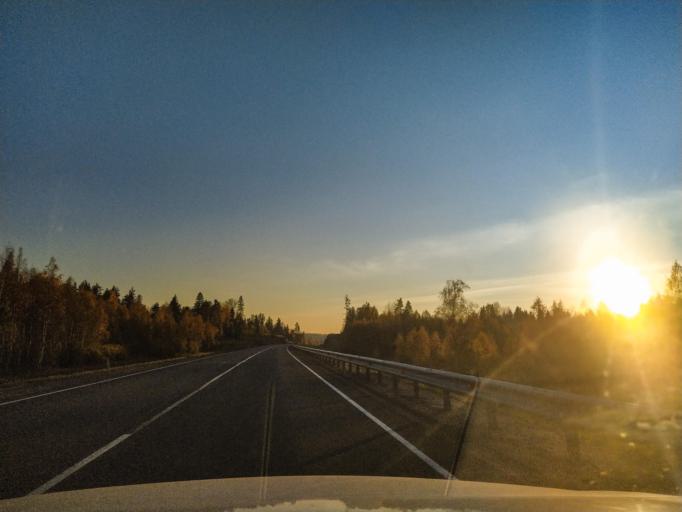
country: RU
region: Leningrad
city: Kuznechnoye
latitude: 61.3479
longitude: 29.8781
